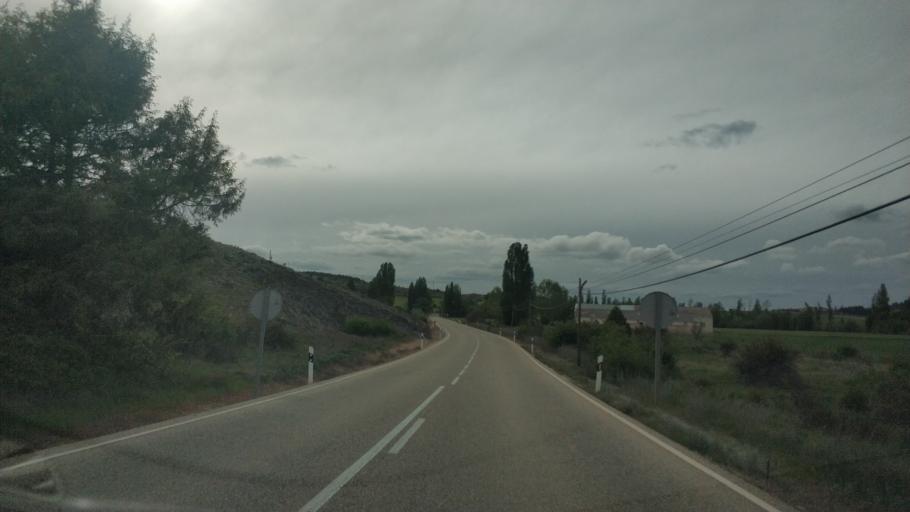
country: ES
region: Castille and Leon
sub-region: Provincia de Soria
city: El Burgo de Osma
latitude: 41.5786
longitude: -3.0336
